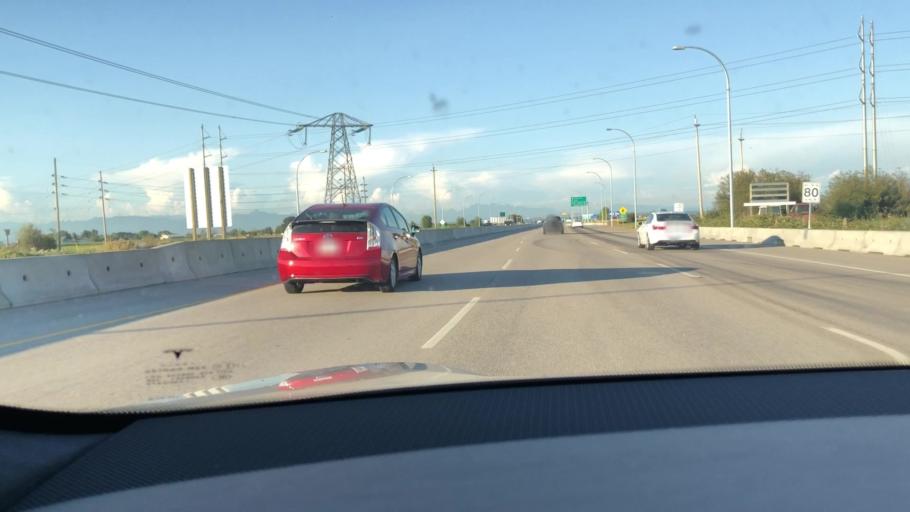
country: CA
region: British Columbia
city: Ladner
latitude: 49.0390
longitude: -123.0766
